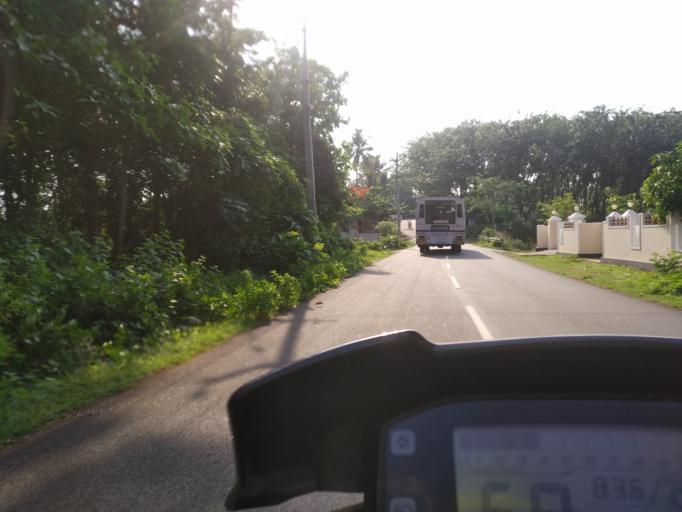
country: IN
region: Kerala
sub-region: Ernakulam
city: Ramamangalam
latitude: 9.9144
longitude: 76.4319
